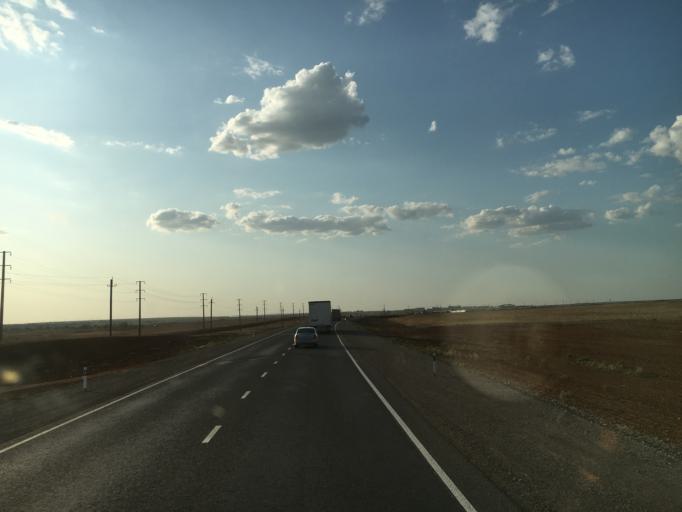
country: KZ
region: Aqtoebe
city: Aqtobe
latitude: 50.2299
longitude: 57.1764
